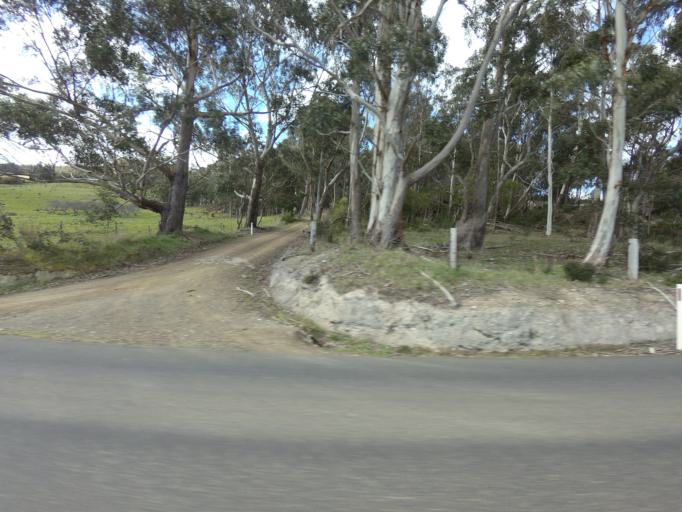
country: AU
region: Tasmania
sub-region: Huon Valley
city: Geeveston
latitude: -43.1884
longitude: 146.9346
